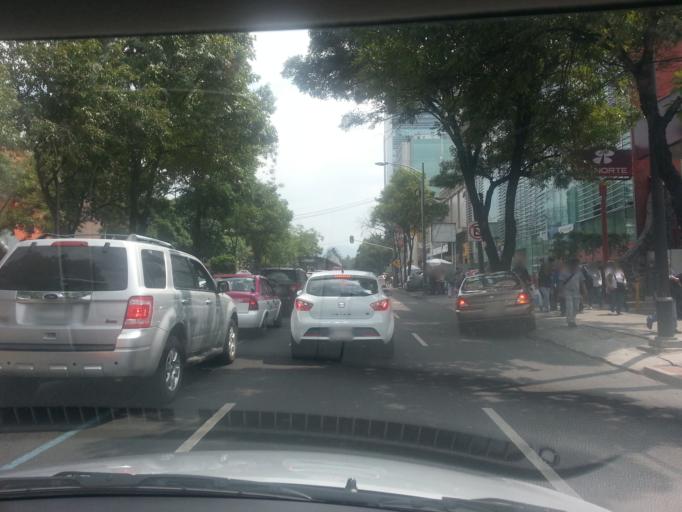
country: MX
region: Mexico City
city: Alvaro Obregon
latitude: 19.3424
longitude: -99.1895
